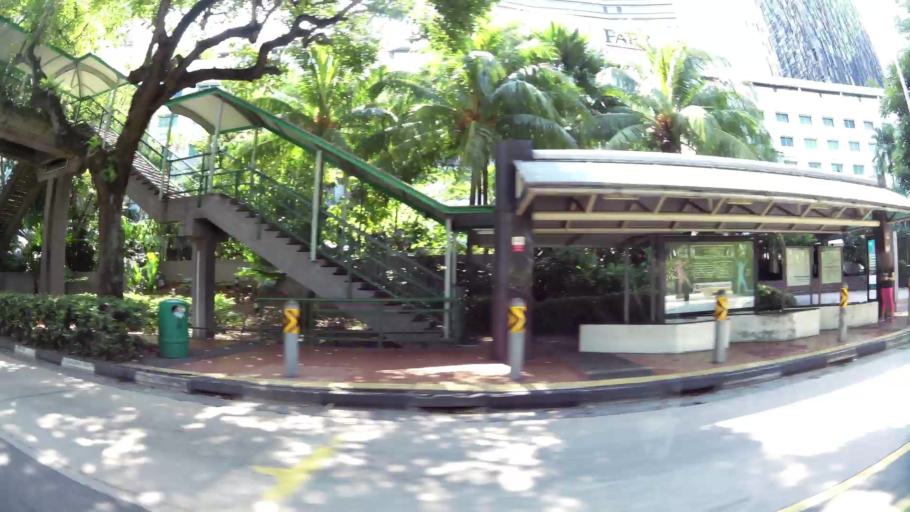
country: SG
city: Singapore
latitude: 1.3005
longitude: 103.8605
